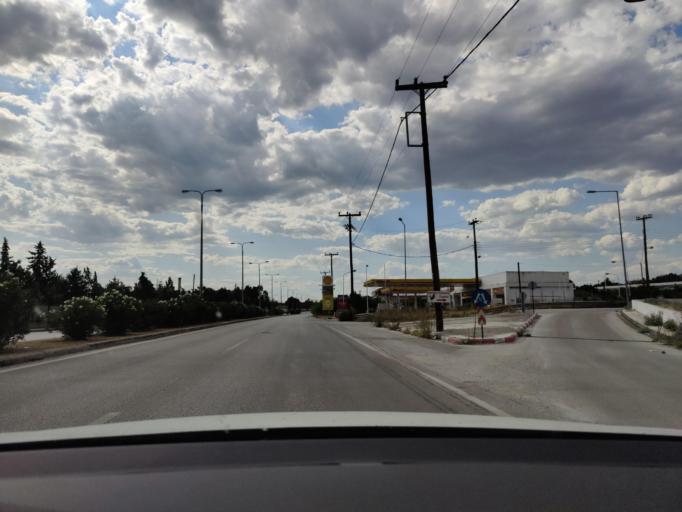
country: GR
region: Central Macedonia
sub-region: Nomos Serron
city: Lefkonas
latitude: 41.0919
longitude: 23.5124
